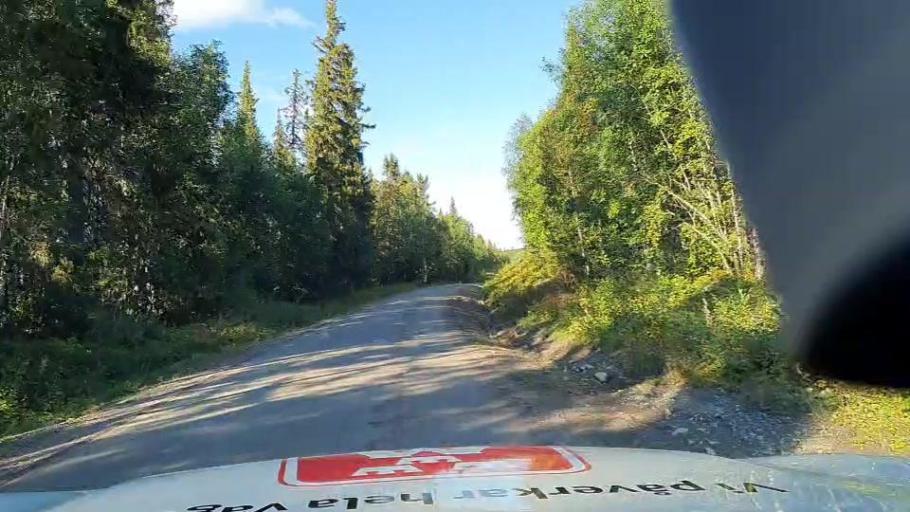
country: SE
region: Jaemtland
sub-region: Stroemsunds Kommun
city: Stroemsund
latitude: 64.5466
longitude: 15.0872
